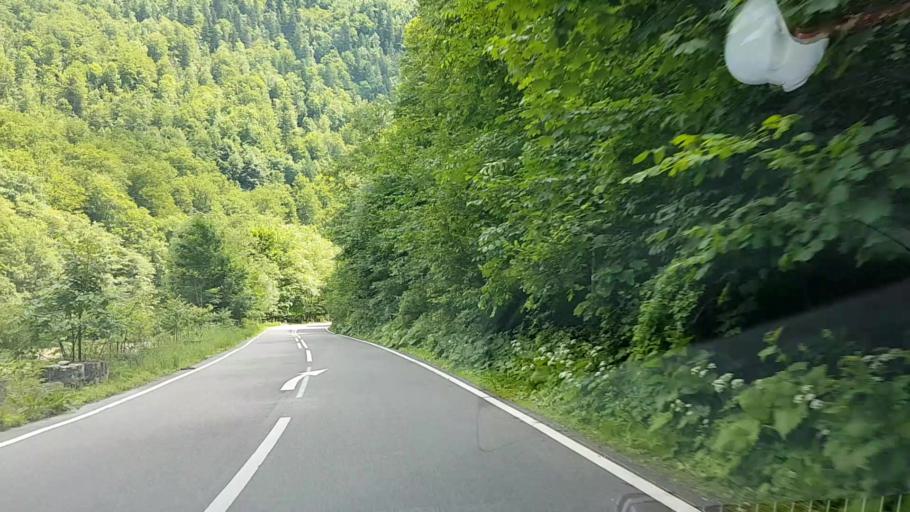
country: RO
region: Suceava
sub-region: Comuna Crucea
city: Crucea
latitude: 47.3126
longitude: 25.6279
